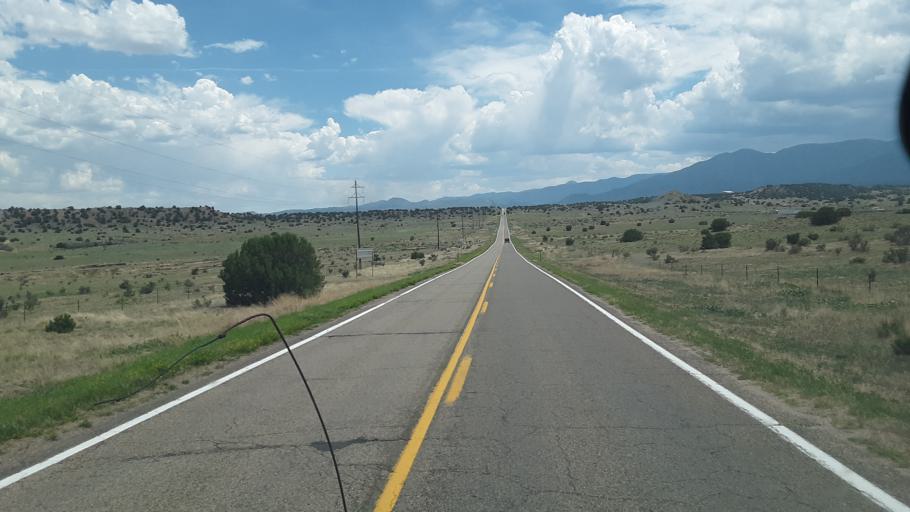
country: US
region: Colorado
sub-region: Fremont County
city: Florence
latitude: 38.3441
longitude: -105.1070
